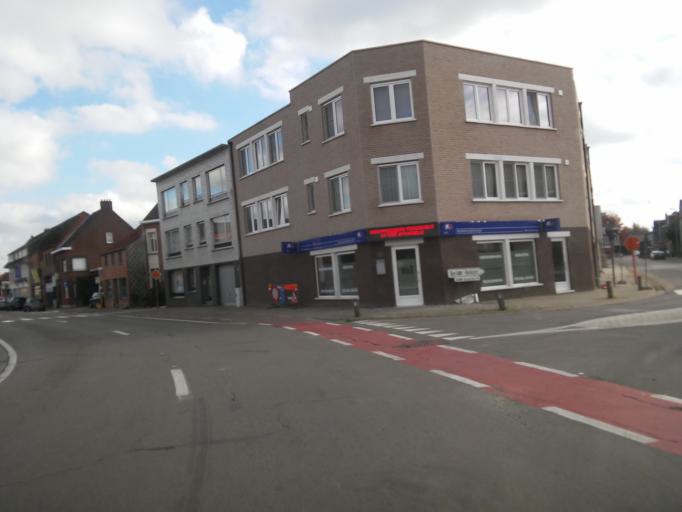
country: BE
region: Flanders
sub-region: Provincie Antwerpen
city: Berlaar
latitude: 51.1173
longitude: 4.6460
